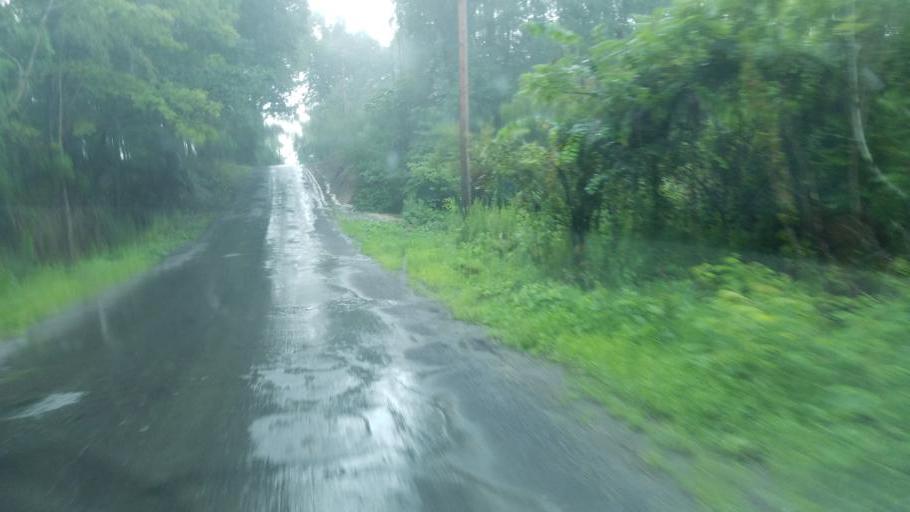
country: US
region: Ohio
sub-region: Geauga County
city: Middlefield
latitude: 41.4836
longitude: -80.9742
